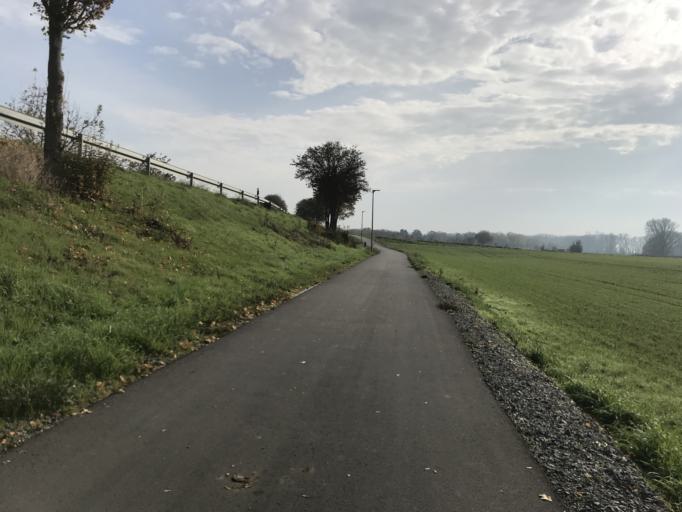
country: DE
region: Hesse
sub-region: Regierungsbezirk Darmstadt
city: Trebur
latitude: 49.9332
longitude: 8.3858
